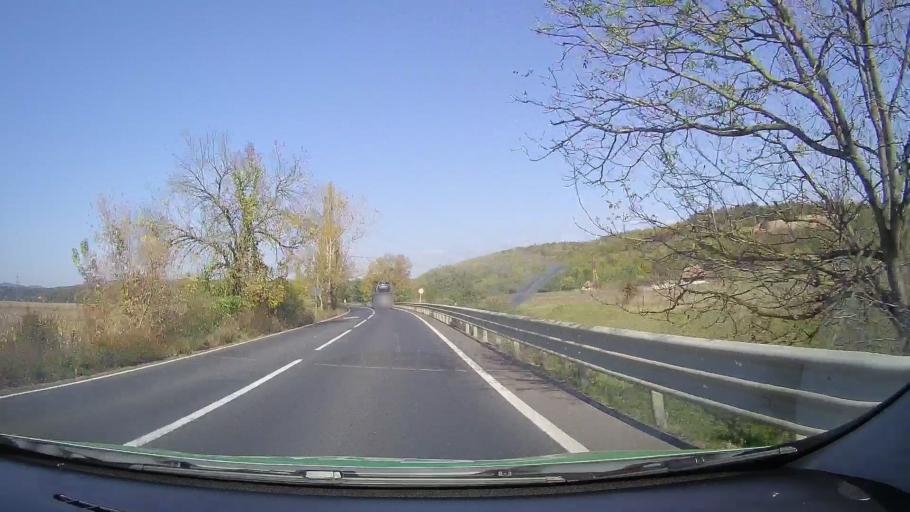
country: RO
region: Arad
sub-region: Comuna Varadia de Mures
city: Varadia de Mures
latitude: 46.0170
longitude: 22.1493
